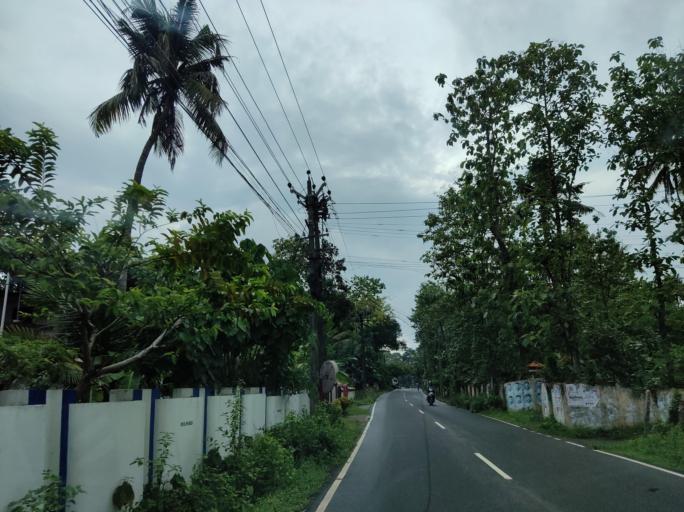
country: IN
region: Kerala
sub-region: Alappuzha
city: Mavelikara
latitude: 9.2302
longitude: 76.5694
